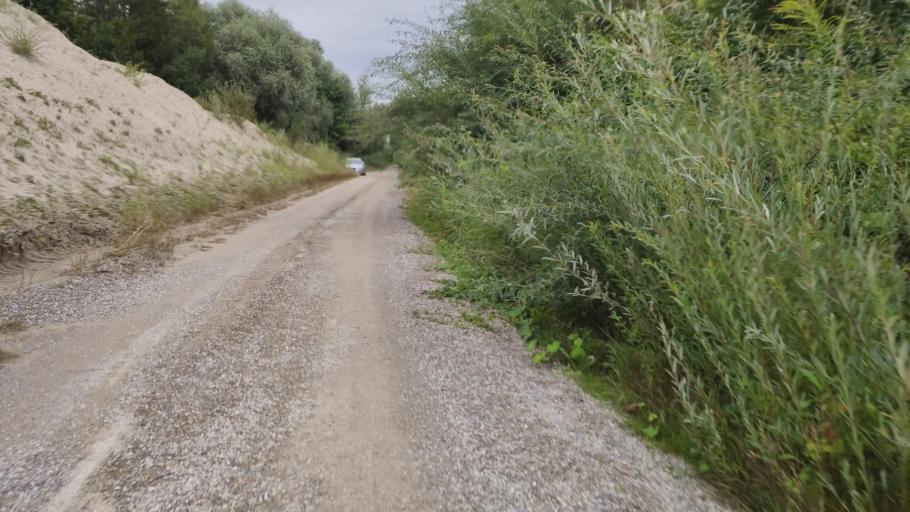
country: DE
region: Bavaria
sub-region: Swabia
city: Konigsbrunn
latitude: 48.2455
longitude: 10.8824
